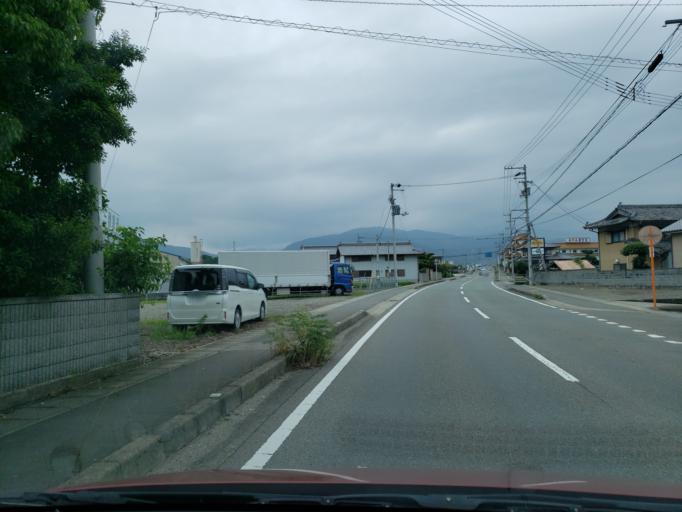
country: JP
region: Tokushima
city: Kamojimacho-jogejima
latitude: 34.1039
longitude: 134.3457
